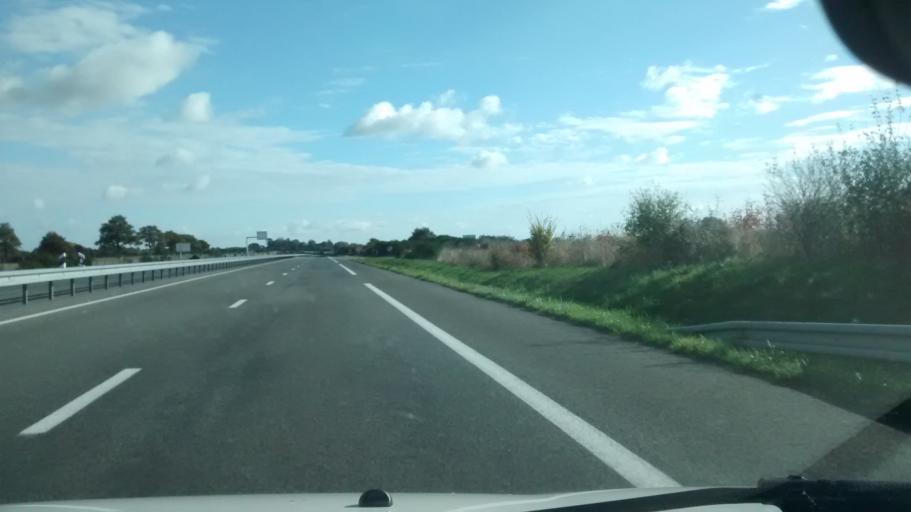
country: FR
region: Pays de la Loire
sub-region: Departement de Maine-et-Loire
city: Pouance
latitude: 47.7297
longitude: -1.1074
